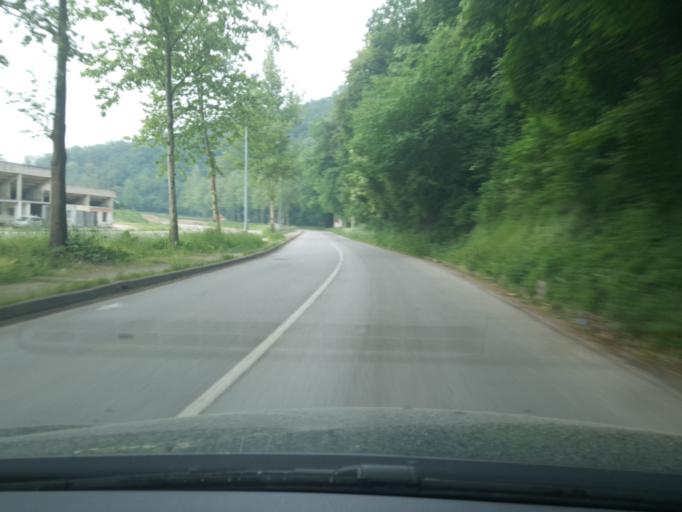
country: RS
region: Central Serbia
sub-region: Kolubarski Okrug
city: Valjevo
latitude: 44.2607
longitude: 19.8744
